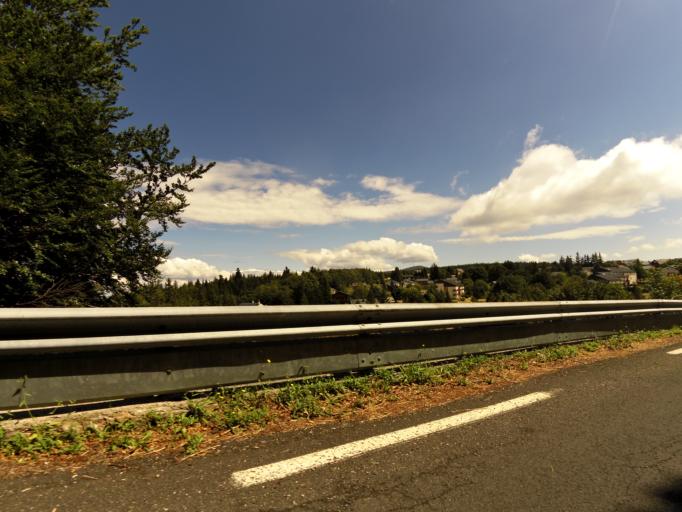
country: FR
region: Languedoc-Roussillon
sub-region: Departement du Gard
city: Valleraugue
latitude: 44.0956
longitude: 3.5492
